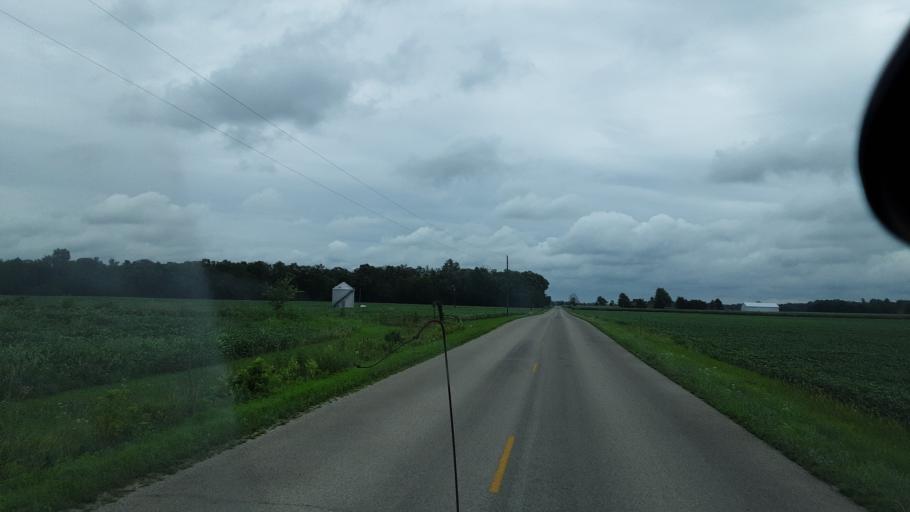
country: US
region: Indiana
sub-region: Jay County
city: Portland
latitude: 40.4821
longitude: -85.0195
